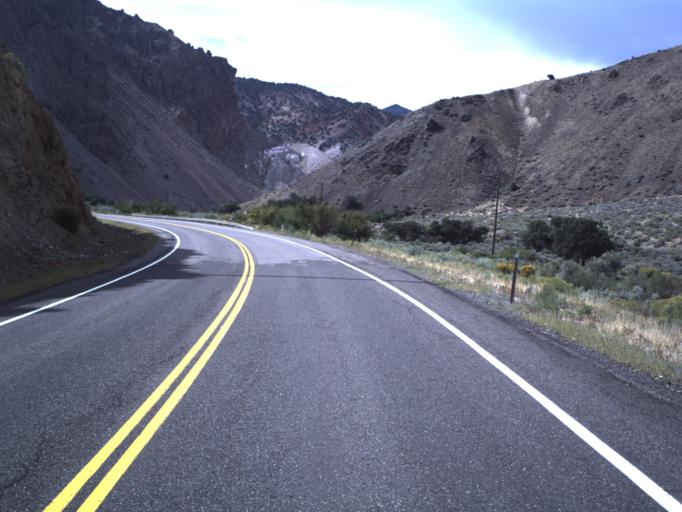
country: US
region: Utah
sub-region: Sevier County
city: Monroe
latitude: 38.4948
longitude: -112.2503
